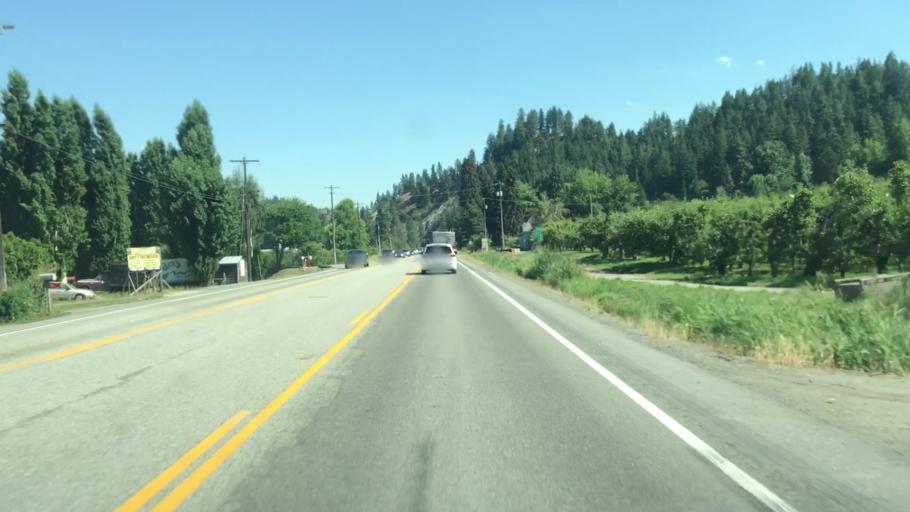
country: US
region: Washington
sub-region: Chelan County
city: Leavenworth
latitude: 47.5864
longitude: -120.6249
